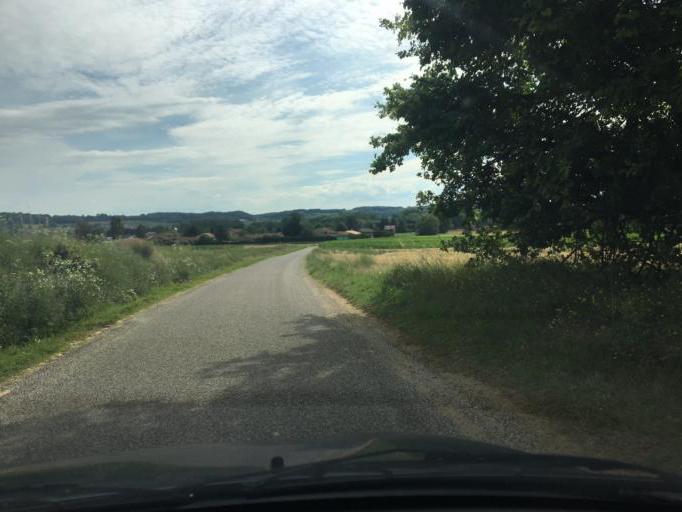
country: FR
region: Rhone-Alpes
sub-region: Departement de la Drome
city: Clerieux
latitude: 45.1122
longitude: 4.9340
